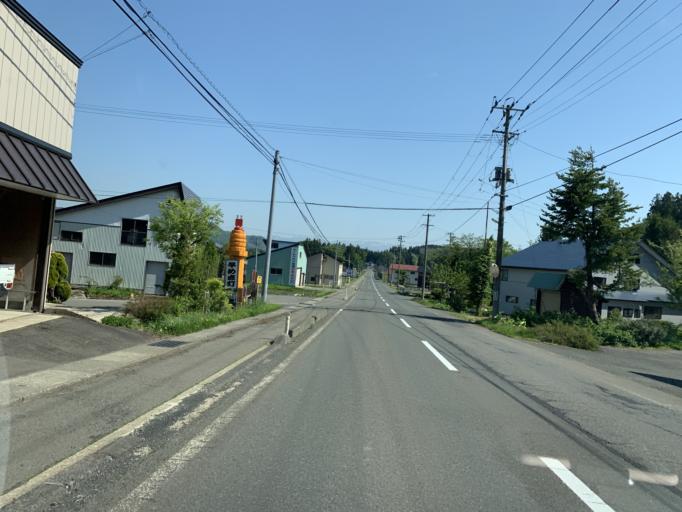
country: JP
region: Akita
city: Yokotemachi
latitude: 39.4159
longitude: 140.7478
